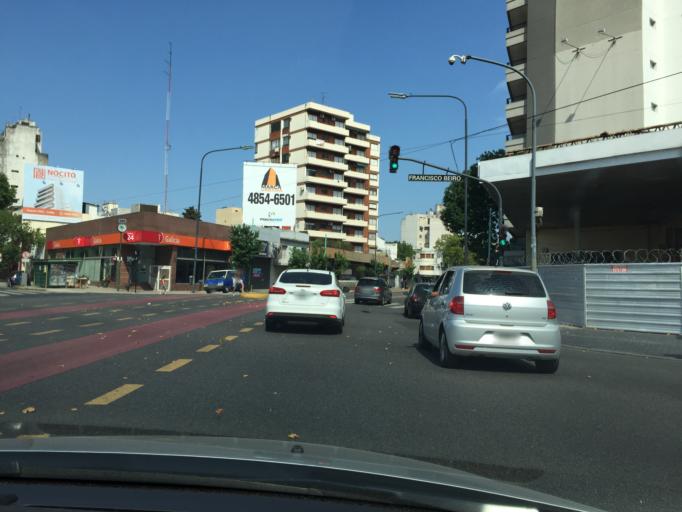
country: AR
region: Buenos Aires F.D.
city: Villa Santa Rita
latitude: -34.5968
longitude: -58.4969
